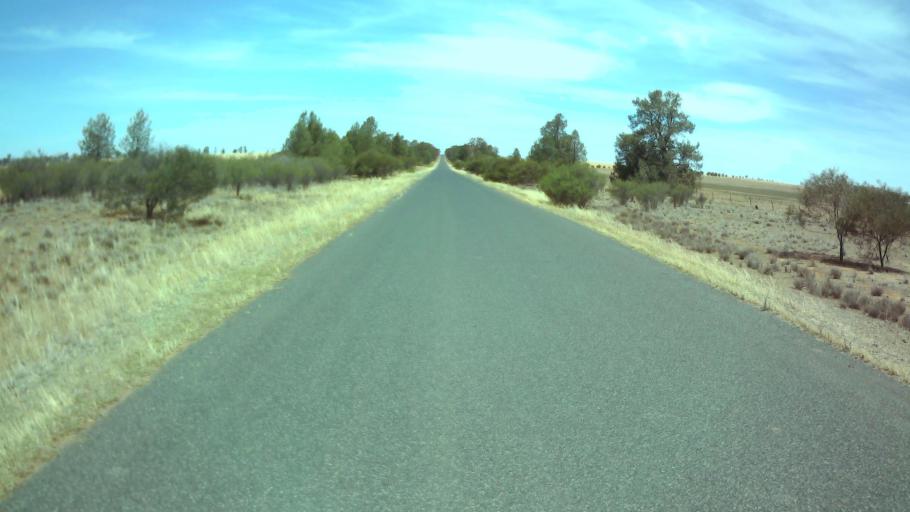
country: AU
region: New South Wales
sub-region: Weddin
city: Grenfell
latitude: -33.8904
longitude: 147.7433
